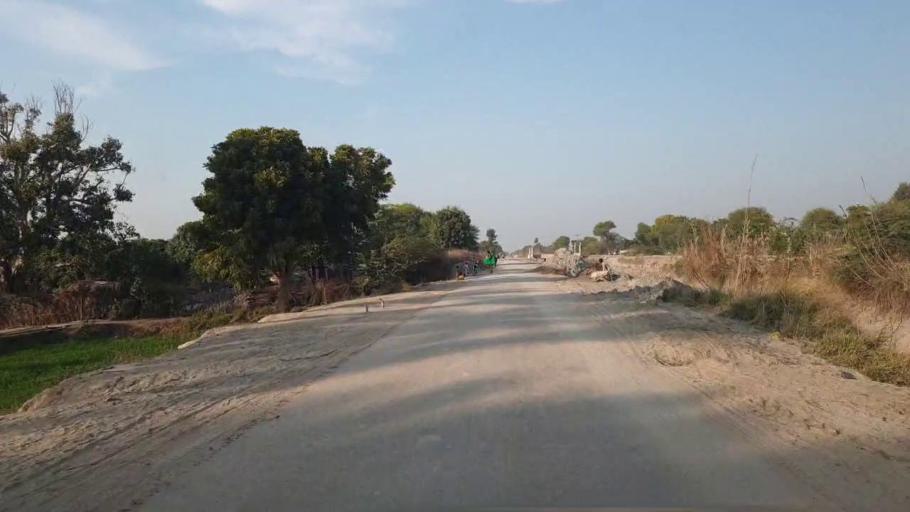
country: PK
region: Sindh
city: Shahpur Chakar
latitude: 26.1559
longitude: 68.6407
